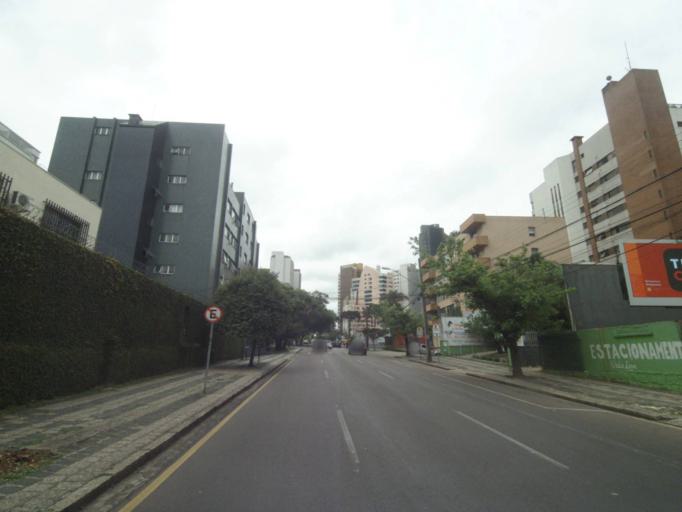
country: BR
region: Parana
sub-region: Curitiba
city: Curitiba
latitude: -25.4333
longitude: -49.2918
